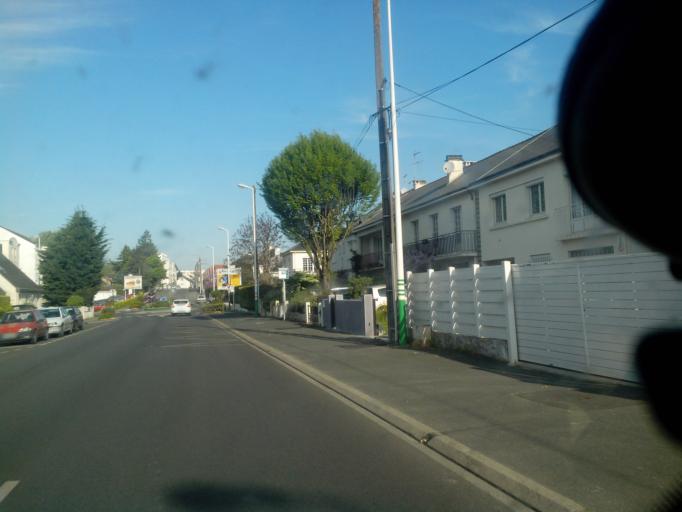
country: FR
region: Pays de la Loire
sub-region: Departement de la Loire-Atlantique
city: Orvault
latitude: 47.2394
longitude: -1.6008
